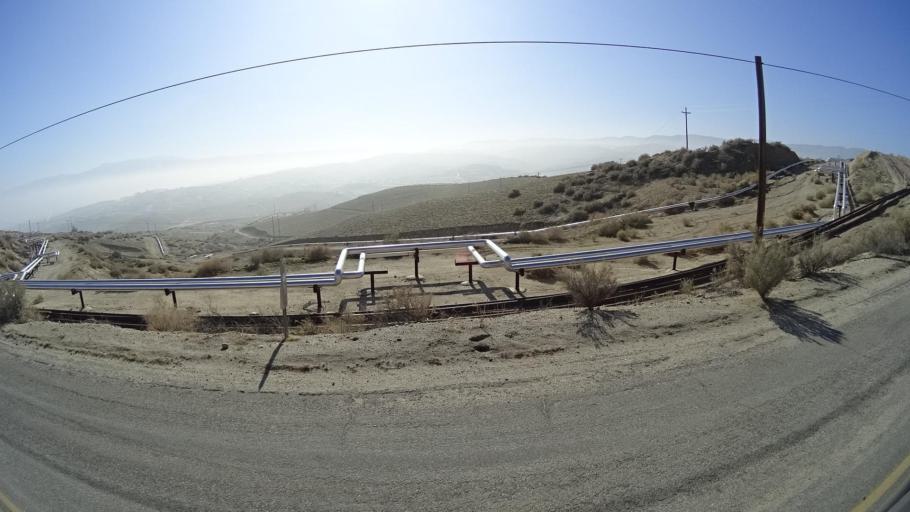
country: US
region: California
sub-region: Kern County
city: South Taft
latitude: 35.1155
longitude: -119.4587
